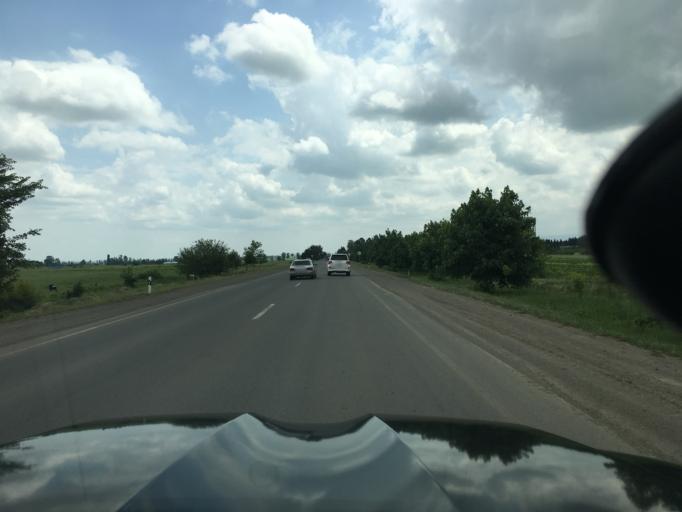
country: AZ
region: Tovuz
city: Tovuz
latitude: 40.9619
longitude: 45.7168
